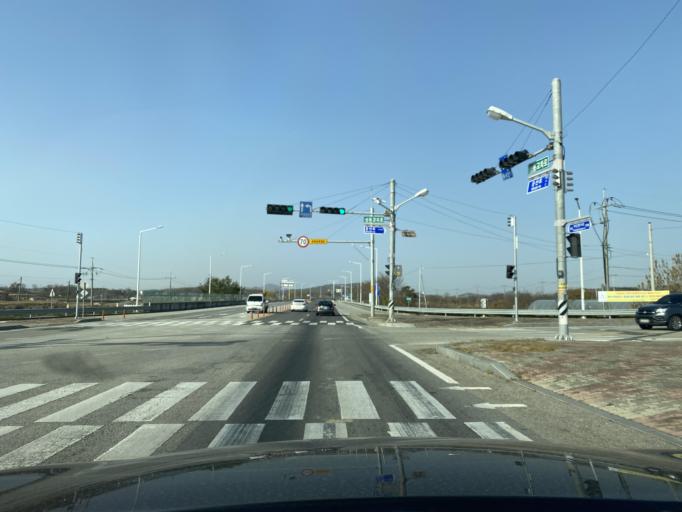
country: KR
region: Chungcheongnam-do
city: Yesan
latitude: 36.7961
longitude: 126.7656
